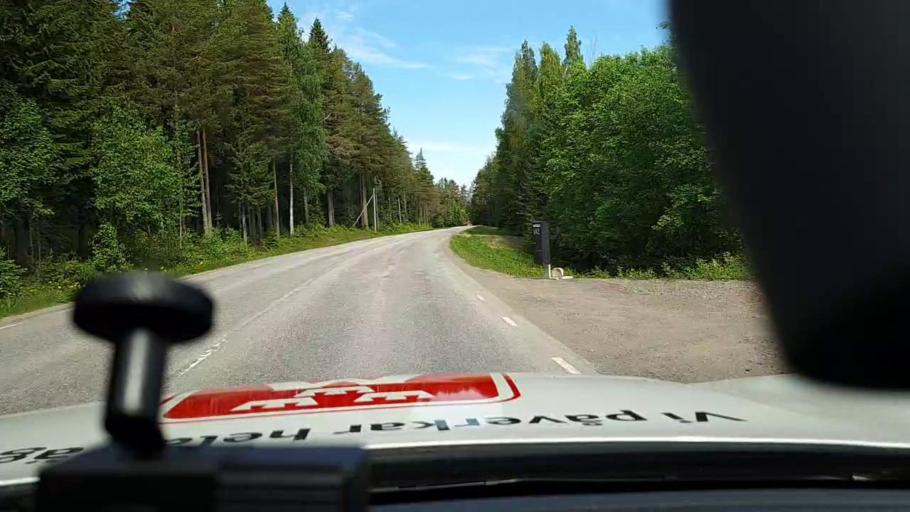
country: SE
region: Norrbotten
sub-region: Lulea Kommun
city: Gammelstad
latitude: 65.5904
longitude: 22.0014
